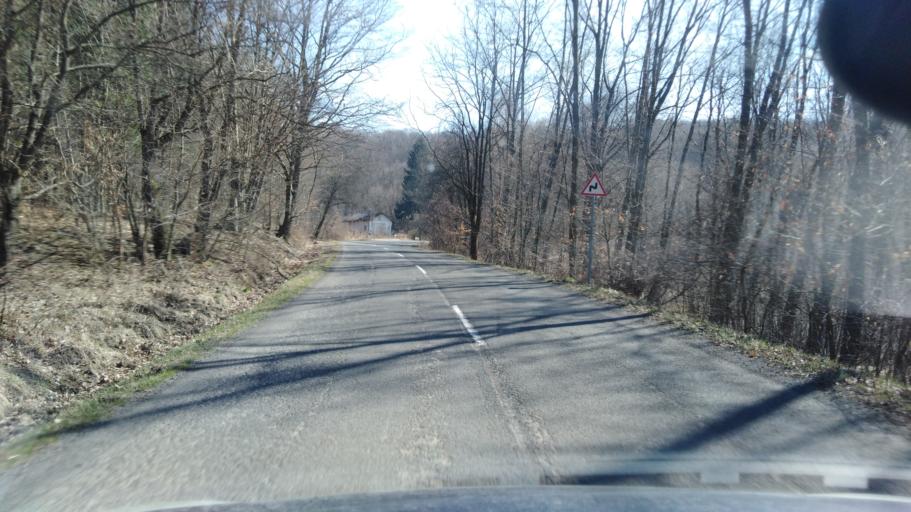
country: HU
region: Nograd
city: Somoskoujfalu
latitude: 48.1520
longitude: 19.8601
